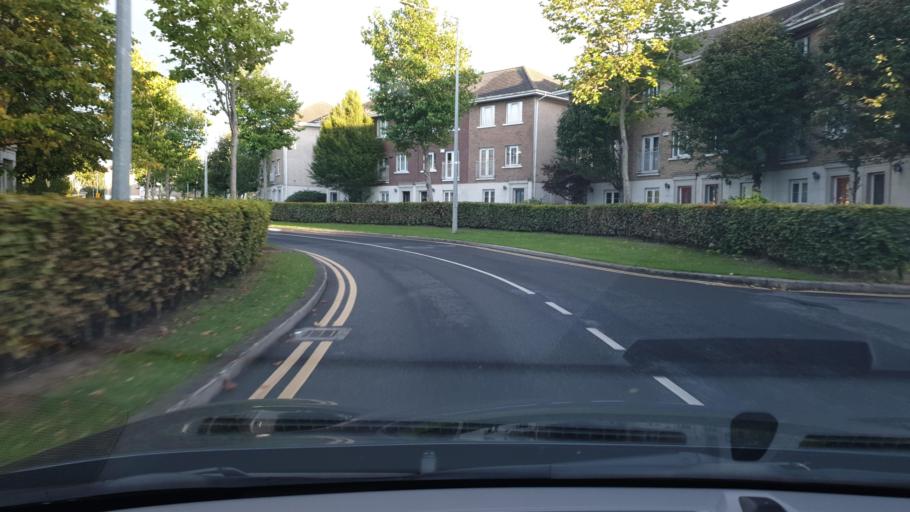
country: IE
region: Leinster
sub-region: Fingal County
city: Blanchardstown
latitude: 53.4213
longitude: -6.3879
